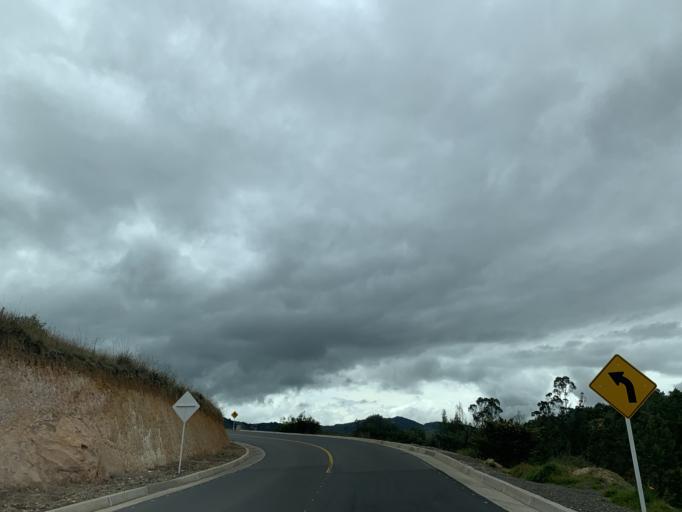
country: CO
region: Boyaca
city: Tunja
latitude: 5.5293
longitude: -73.3226
